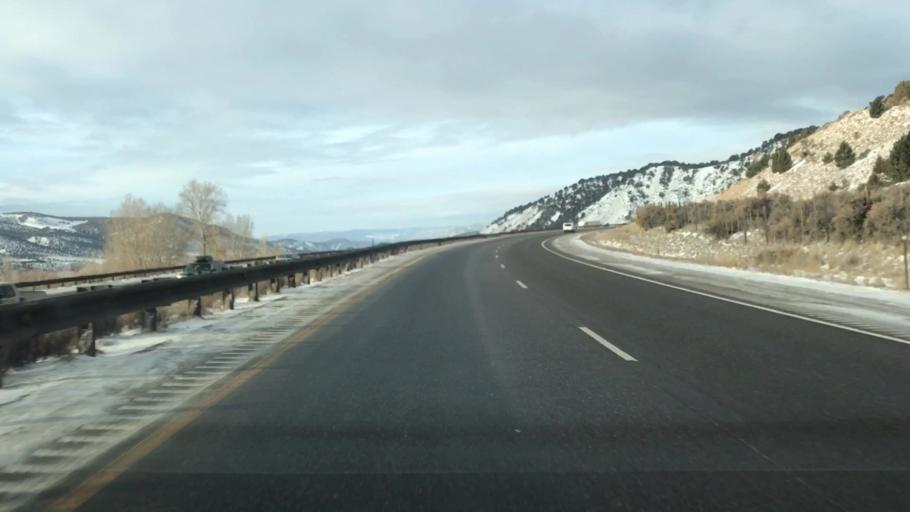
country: US
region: Colorado
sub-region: Eagle County
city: Eagle
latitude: 39.6798
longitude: -106.7668
